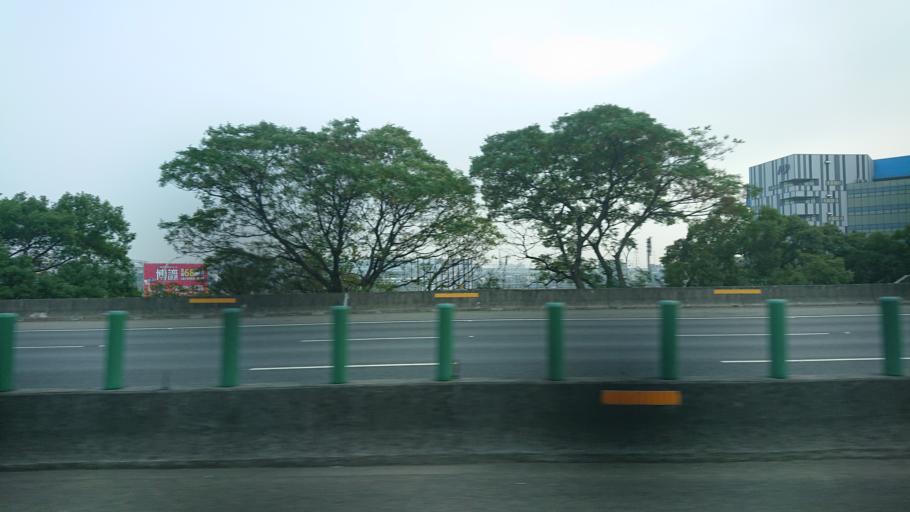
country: TW
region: Taiwan
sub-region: Changhua
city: Chang-hua
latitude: 24.1136
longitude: 120.6095
